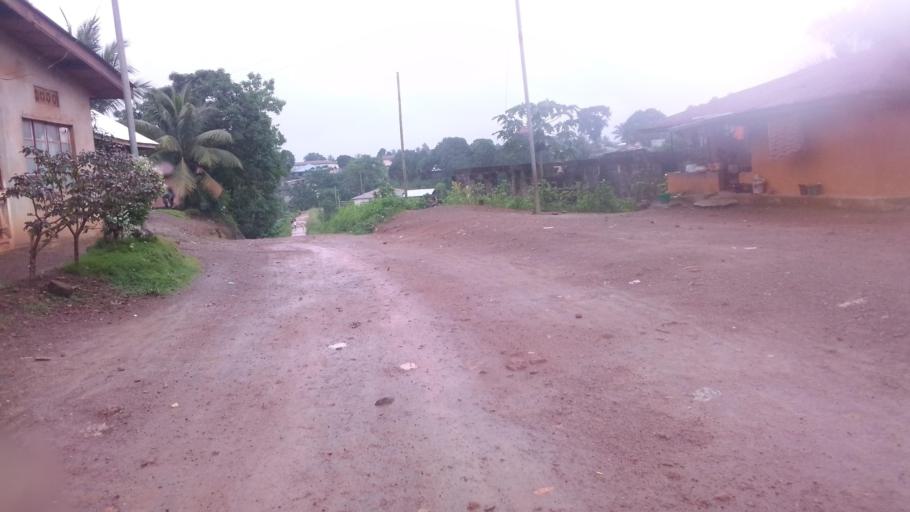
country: SL
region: Eastern Province
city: Kenema
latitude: 7.8887
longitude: -11.1775
